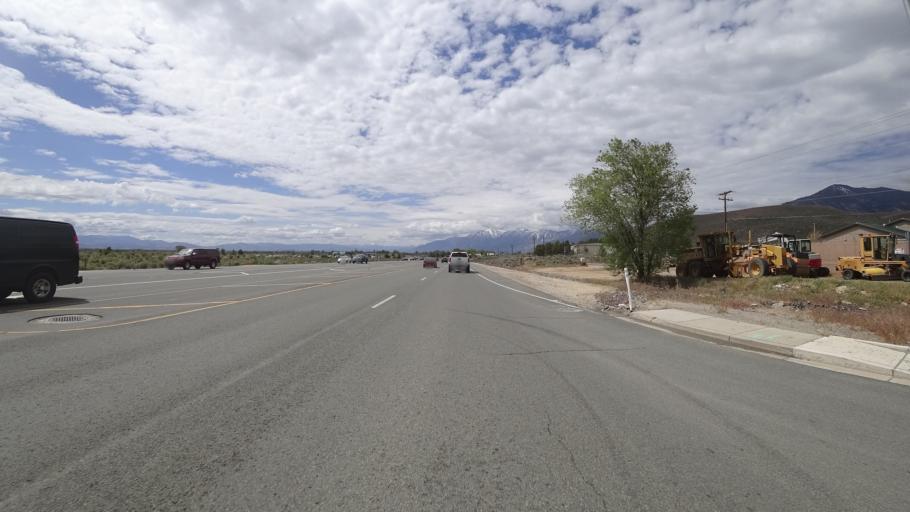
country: US
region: Nevada
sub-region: Douglas County
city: Indian Hills
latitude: 39.0741
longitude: -119.7795
